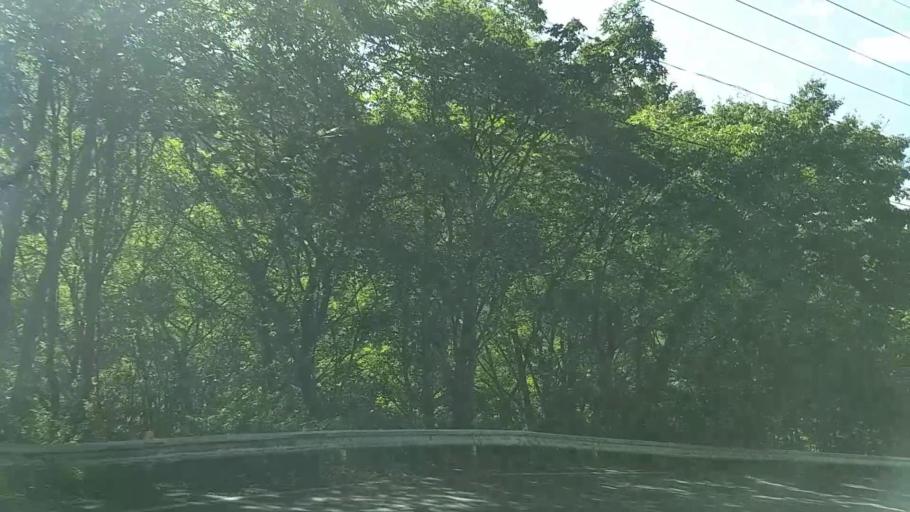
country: JP
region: Nagano
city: Matsumoto
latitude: 36.2062
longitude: 138.0953
